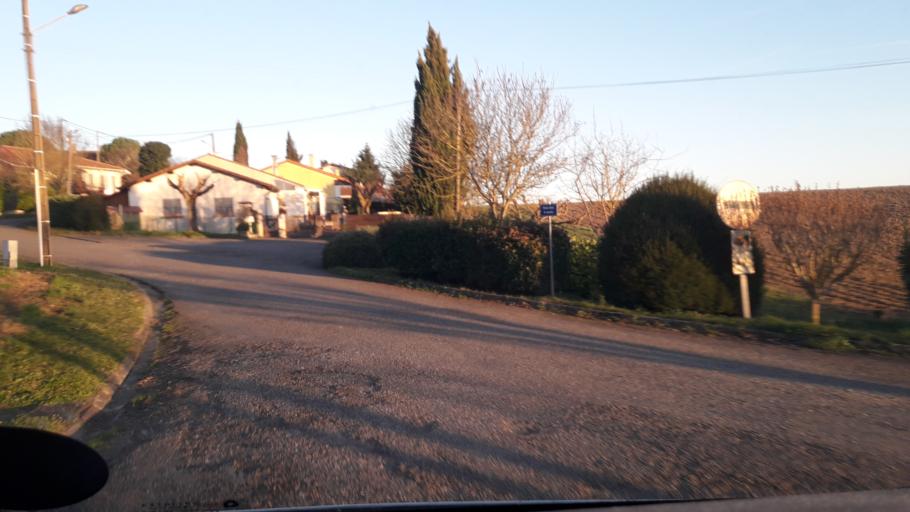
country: FR
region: Midi-Pyrenees
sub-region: Departement du Gers
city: Gimont
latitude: 43.5963
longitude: 0.9825
